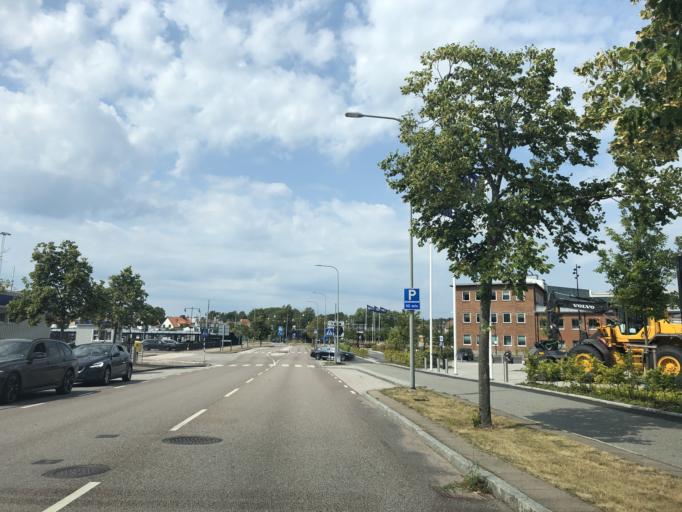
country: SE
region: Vaestra Goetaland
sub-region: Goteborg
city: Majorna
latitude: 57.7167
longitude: 11.9219
